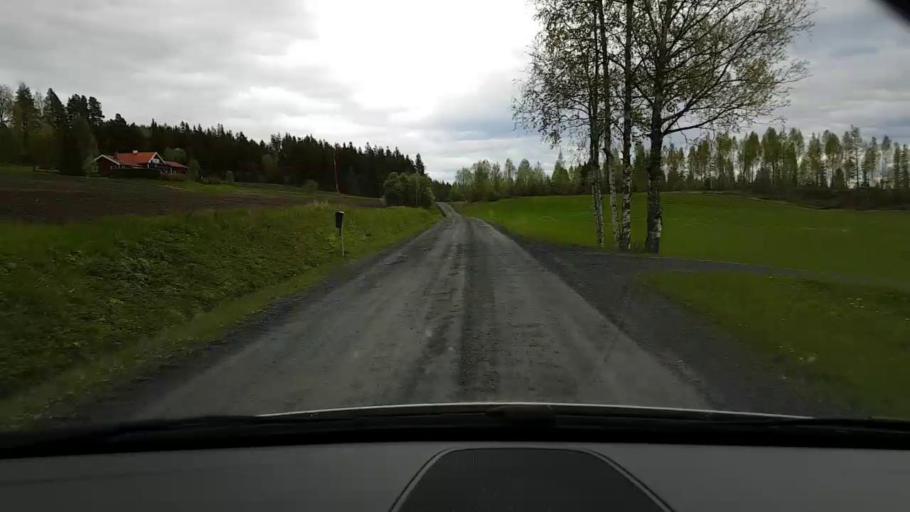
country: SE
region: Jaemtland
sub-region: Krokoms Kommun
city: Valla
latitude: 63.3033
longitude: 13.9598
